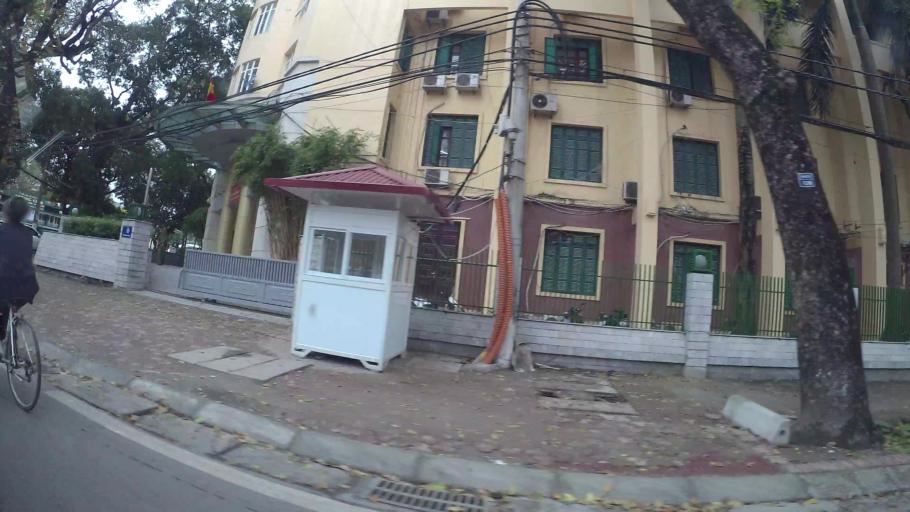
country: VN
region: Ha Noi
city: Hai BaTrung
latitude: 21.0178
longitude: 105.8436
